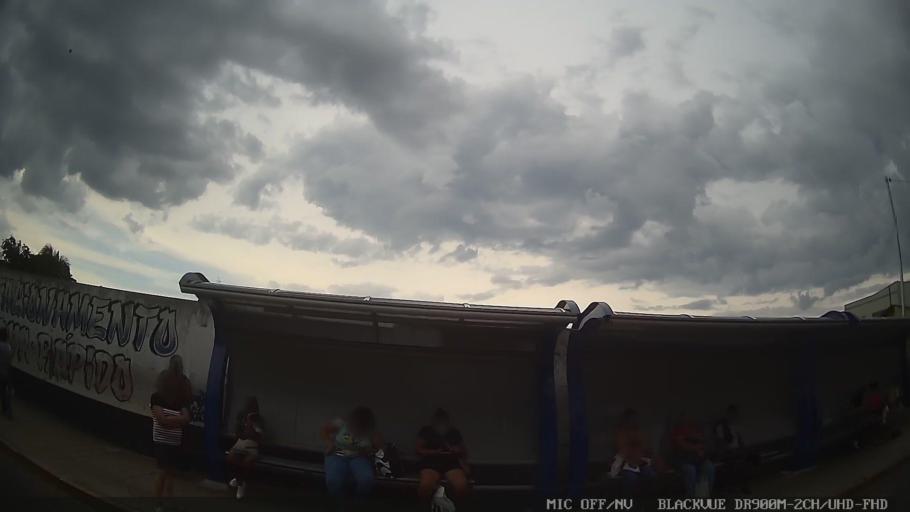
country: BR
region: Sao Paulo
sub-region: Atibaia
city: Atibaia
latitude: -23.1143
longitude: -46.5514
